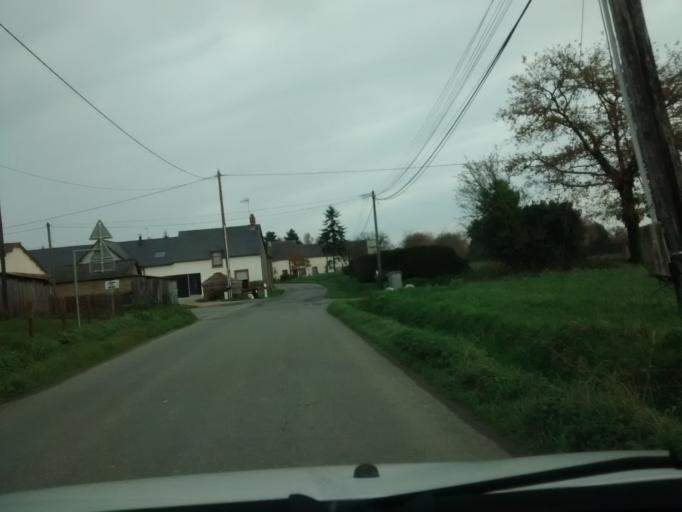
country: FR
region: Brittany
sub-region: Departement d'Ille-et-Vilaine
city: Noyal-sur-Vilaine
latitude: 48.1029
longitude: -1.5337
